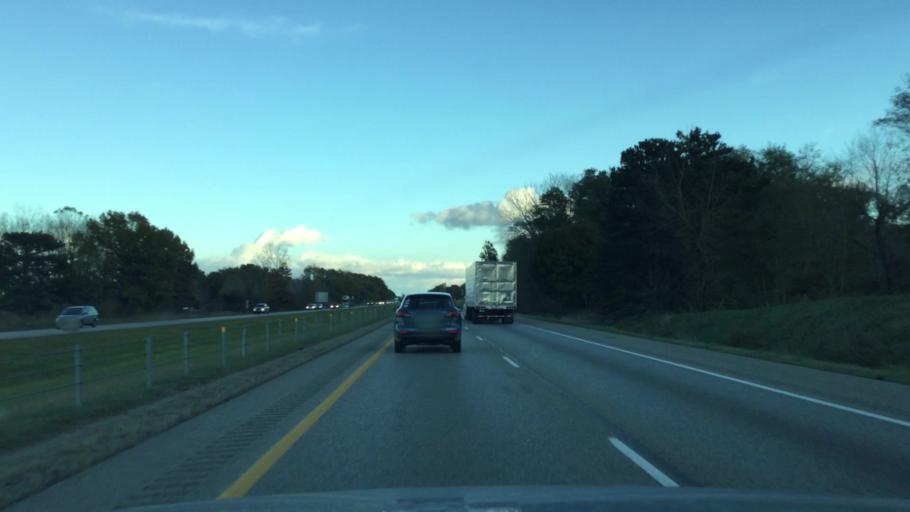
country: US
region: Michigan
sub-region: Calhoun County
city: Springfield
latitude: 42.2682
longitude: -85.2729
